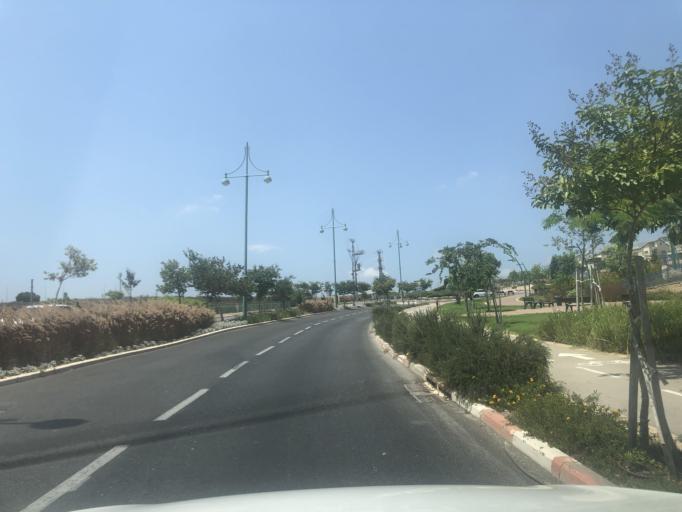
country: IL
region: Haifa
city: Daliyat el Karmil
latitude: 32.6343
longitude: 35.0793
